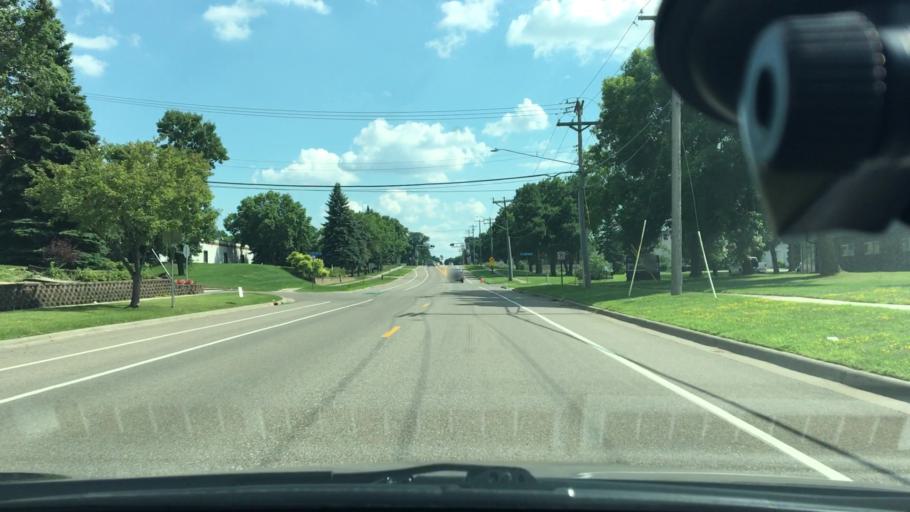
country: US
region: Minnesota
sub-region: Hennepin County
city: New Hope
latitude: 45.0515
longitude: -93.3907
